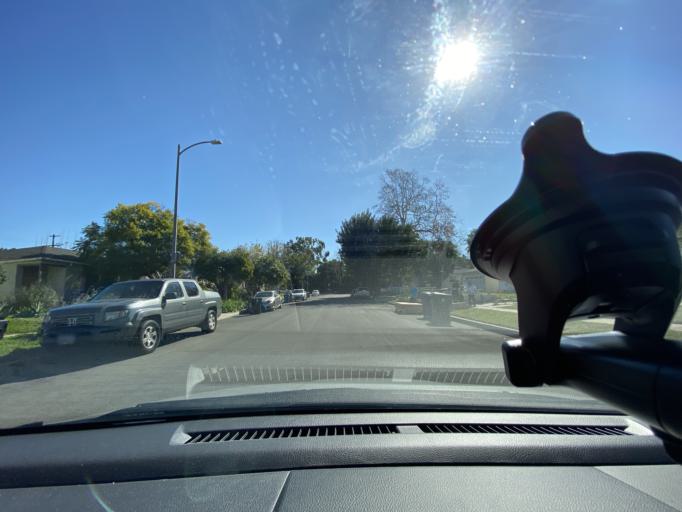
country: US
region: California
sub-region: Los Angeles County
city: Century City
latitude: 34.0329
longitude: -118.4252
